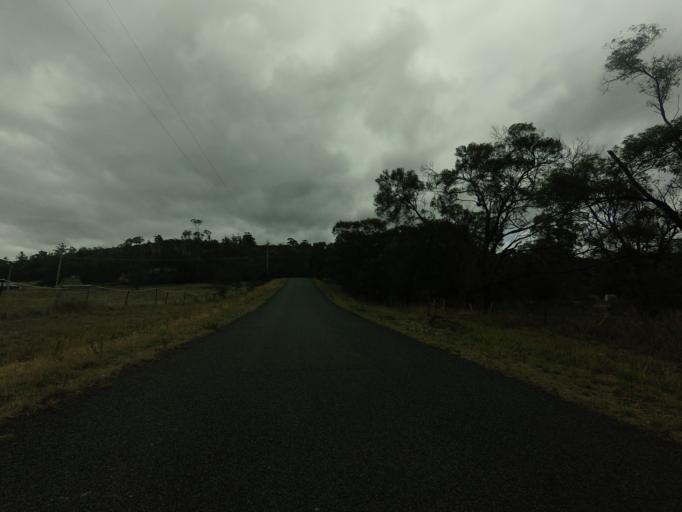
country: AU
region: Tasmania
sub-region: Clarence
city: Cambridge
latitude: -42.7833
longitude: 147.4077
